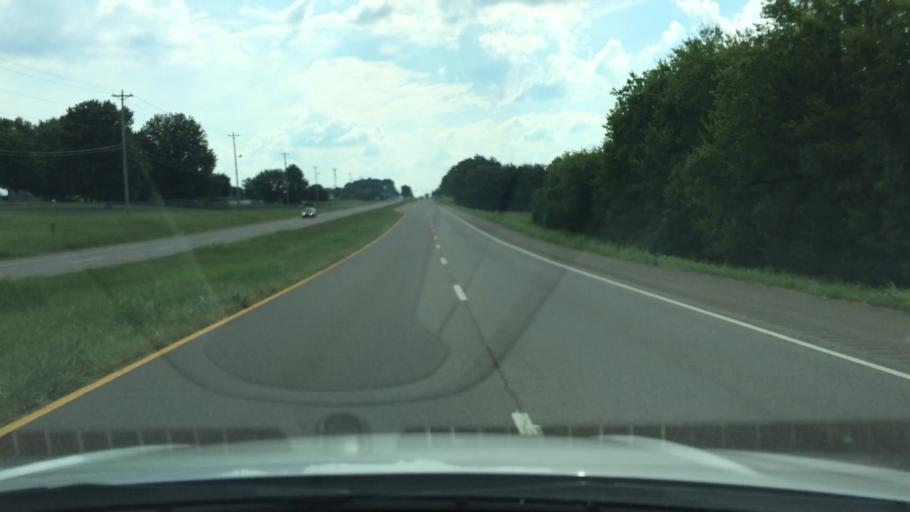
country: US
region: Tennessee
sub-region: Jefferson County
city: Jefferson City
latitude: 36.1116
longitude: -83.5081
